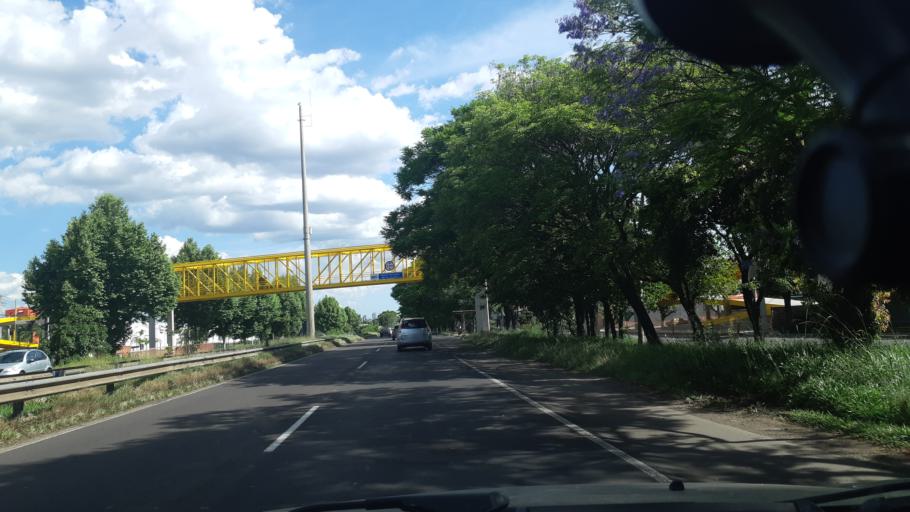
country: BR
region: Rio Grande do Sul
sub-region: Novo Hamburgo
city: Novo Hamburgo
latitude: -29.6624
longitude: -51.1439
